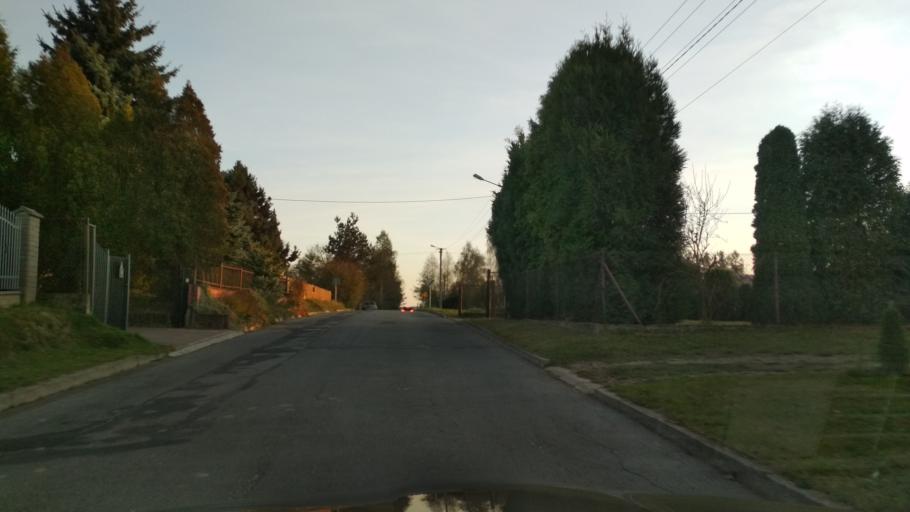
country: PL
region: Subcarpathian Voivodeship
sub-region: Powiat ropczycko-sedziszowski
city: Sedziszow Malopolski
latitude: 50.0639
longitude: 21.7114
